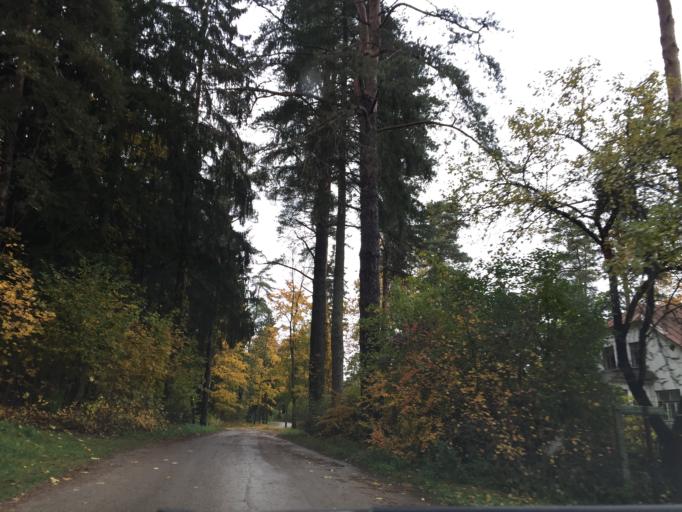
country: LV
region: Ogre
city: Ogre
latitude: 56.8088
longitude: 24.6299
